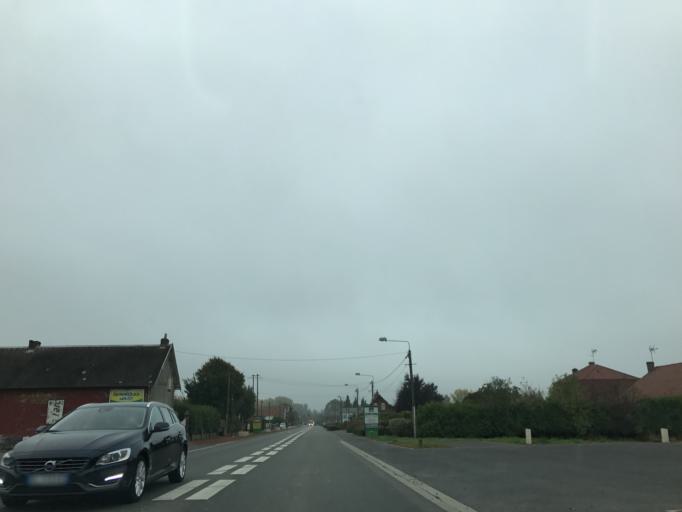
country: FR
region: Nord-Pas-de-Calais
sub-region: Departement du Pas-de-Calais
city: Beaurains
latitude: 50.2202
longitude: 2.8104
